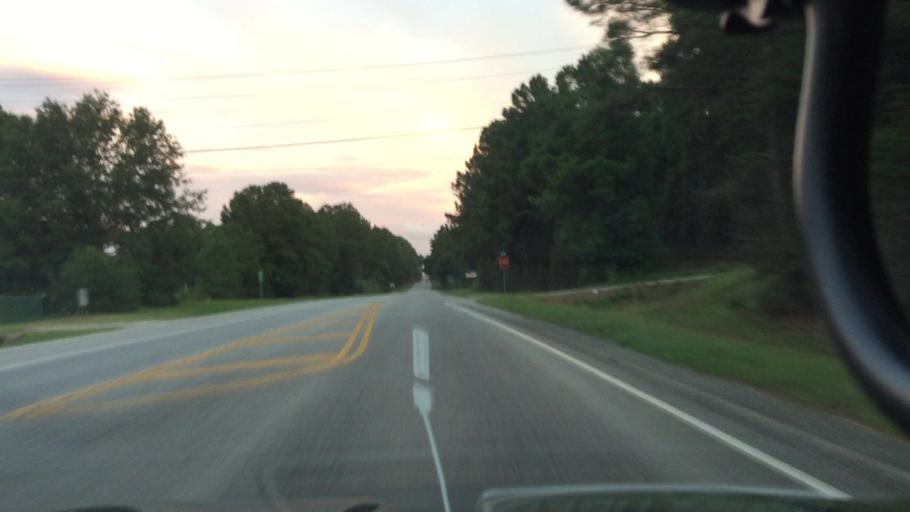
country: US
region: Alabama
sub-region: Coffee County
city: New Brockton
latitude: 31.3937
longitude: -85.8783
